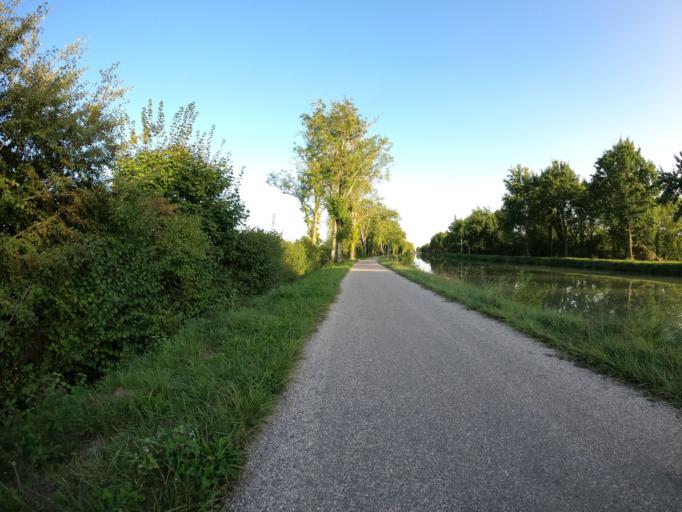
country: FR
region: Midi-Pyrenees
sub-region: Departement du Tarn-et-Garonne
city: Saint-Porquier
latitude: 44.0229
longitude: 1.1637
